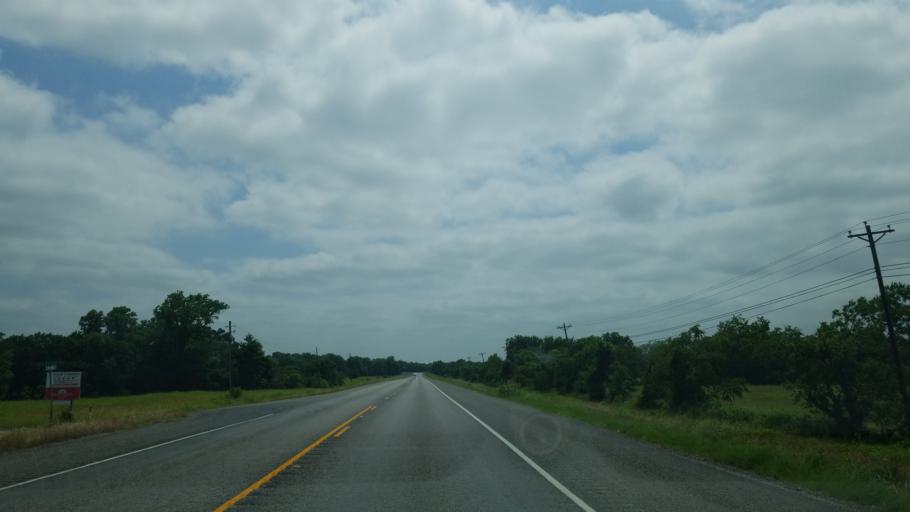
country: US
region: Texas
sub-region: Denton County
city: Denton
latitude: 33.2886
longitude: -97.0847
